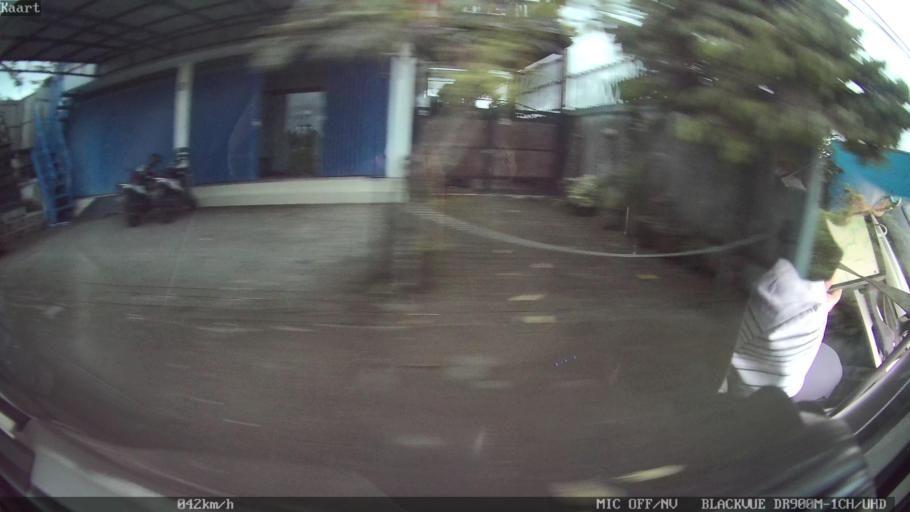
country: ID
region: Bali
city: Banjar Mambalkajanan
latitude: -8.5394
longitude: 115.2235
